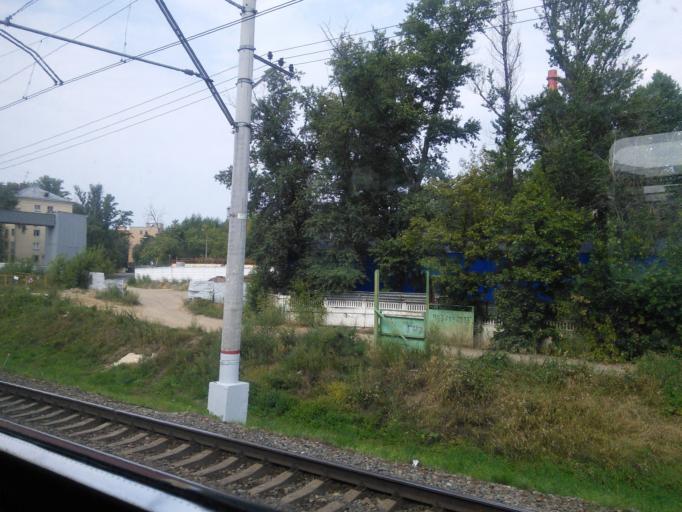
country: RU
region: Moscow
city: Lefortovo
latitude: 55.7484
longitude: 37.7278
